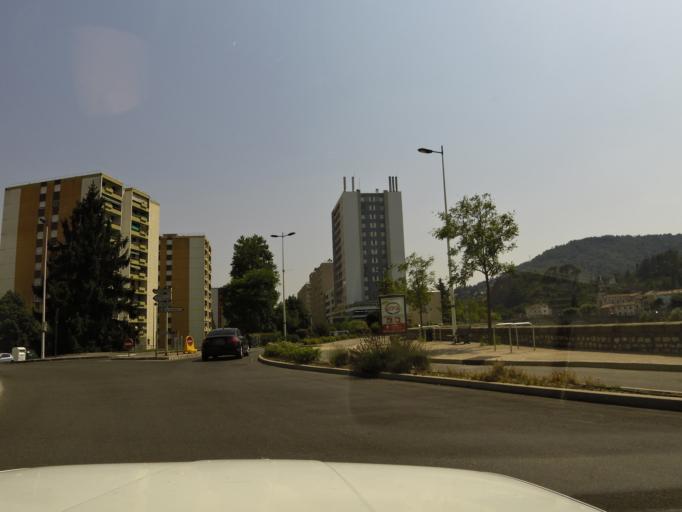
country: FR
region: Languedoc-Roussillon
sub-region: Departement du Gard
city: Ales
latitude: 44.1268
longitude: 4.0732
